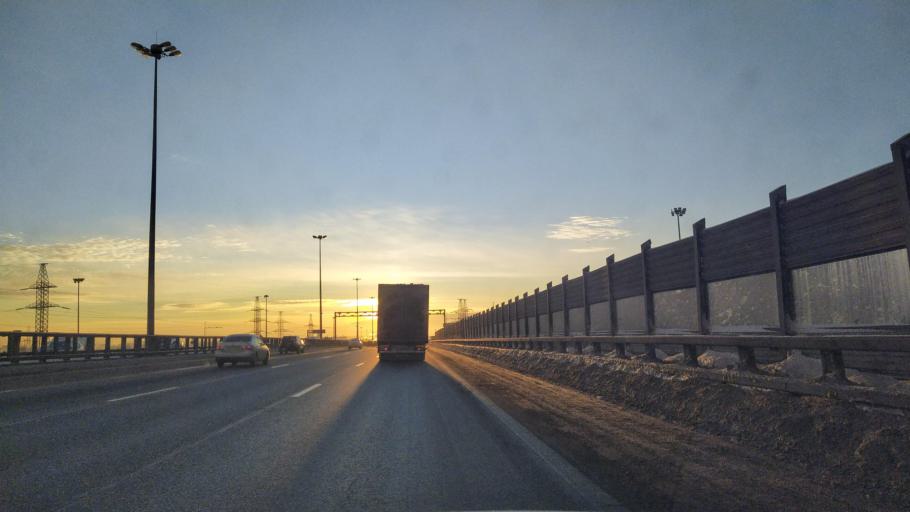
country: RU
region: St.-Petersburg
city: Obukhovo
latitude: 59.8311
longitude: 30.4423
